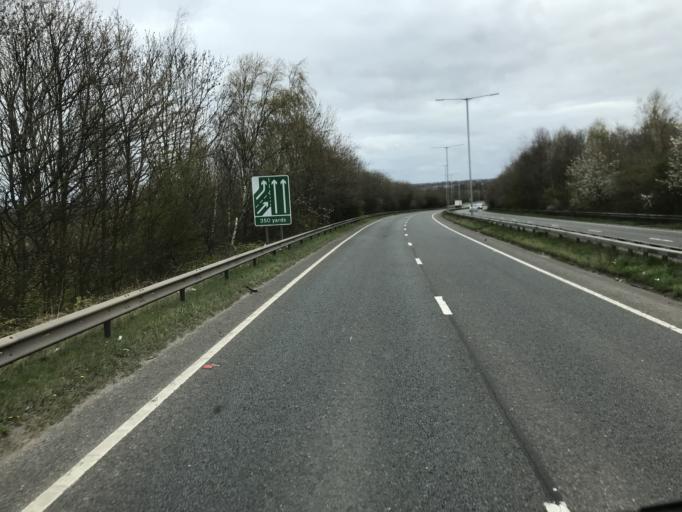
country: GB
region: England
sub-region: Borough of Halton
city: Hale
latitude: 53.3556
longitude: -2.8087
